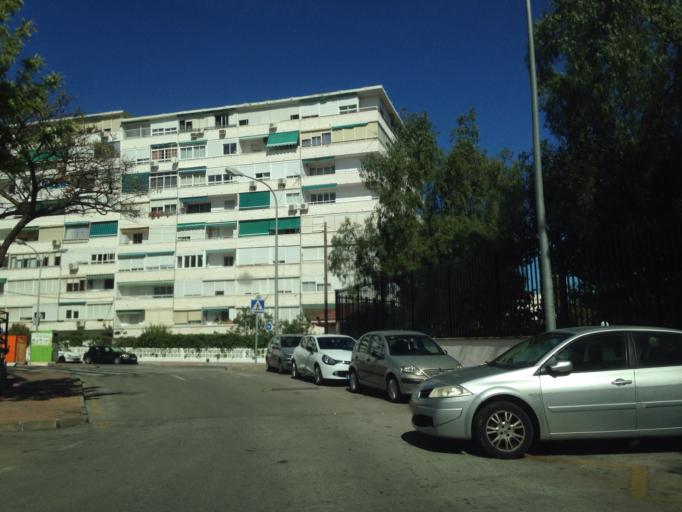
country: ES
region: Andalusia
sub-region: Provincia de Malaga
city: Benalmadena
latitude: 36.5969
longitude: -4.5395
